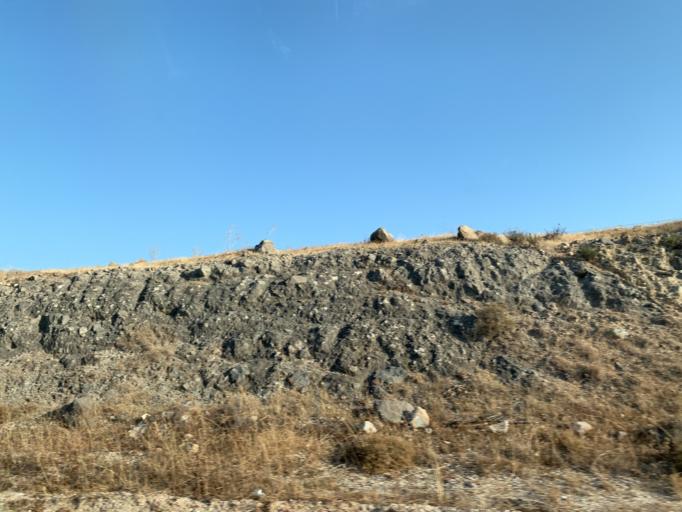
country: TR
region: Izmir
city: Alacati
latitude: 38.2775
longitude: 26.4254
